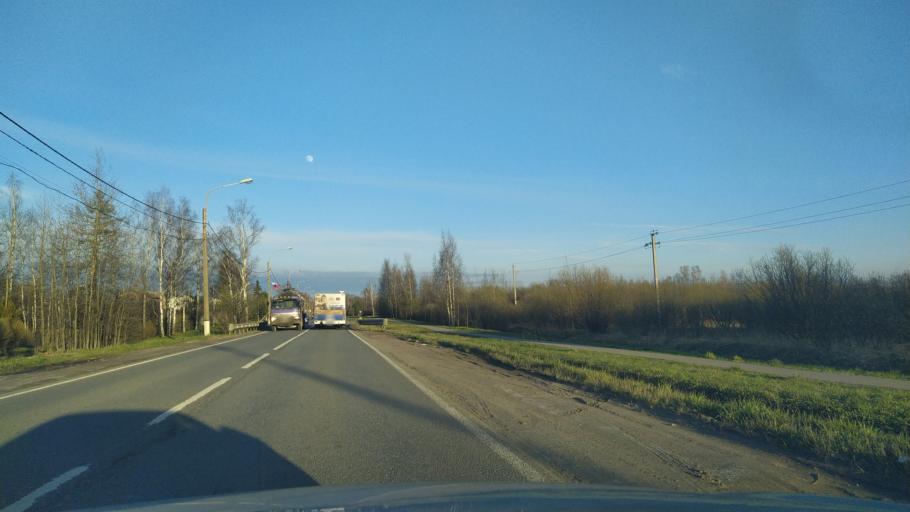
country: RU
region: St.-Petersburg
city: Aleksandrovskaya
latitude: 59.7378
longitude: 30.3249
